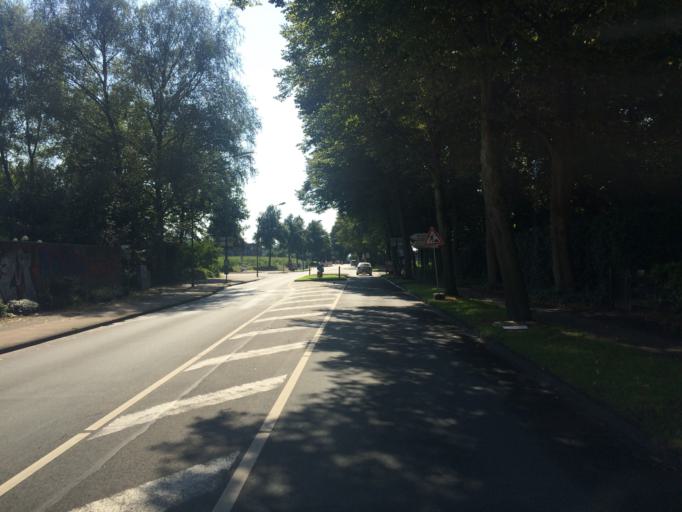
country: DE
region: North Rhine-Westphalia
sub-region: Regierungsbezirk Munster
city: Muenster
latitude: 51.9822
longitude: 7.7026
